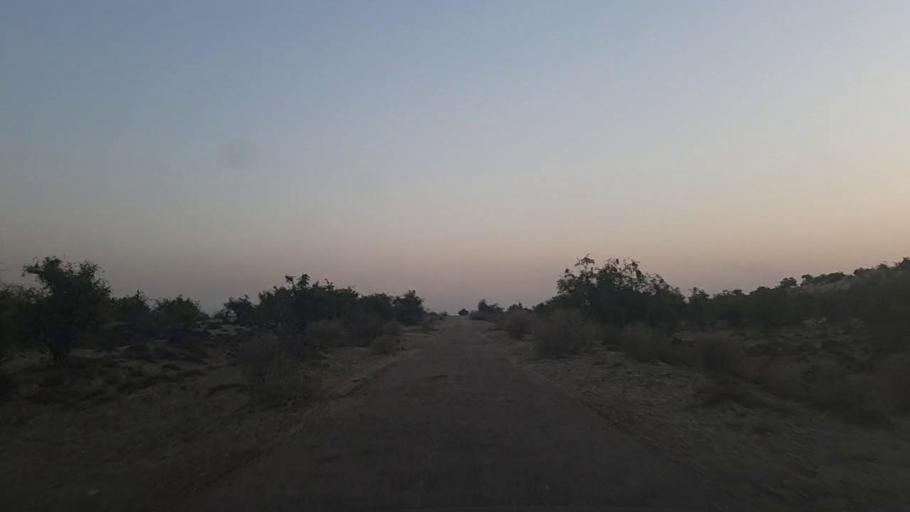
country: PK
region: Sindh
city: Jam Sahib
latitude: 26.4094
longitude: 68.8095
